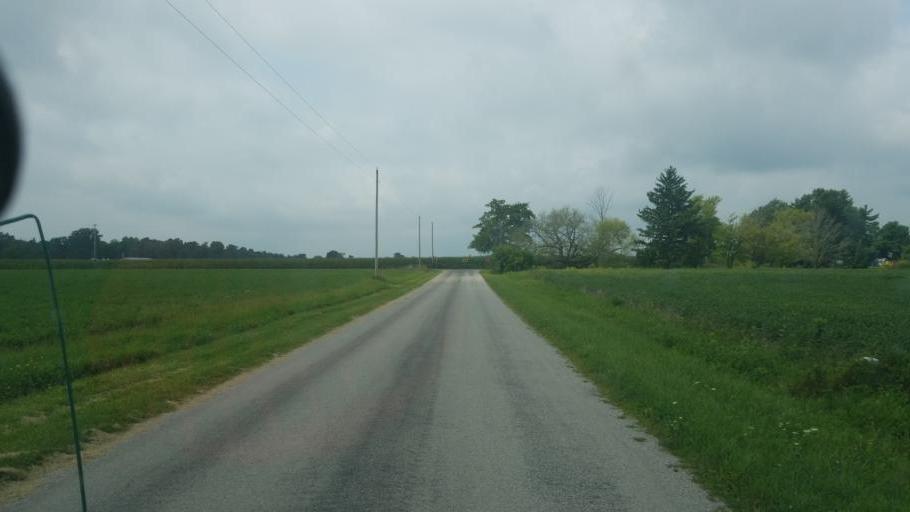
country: US
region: Ohio
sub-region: Huron County
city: Greenwich
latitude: 41.0108
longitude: -82.5081
